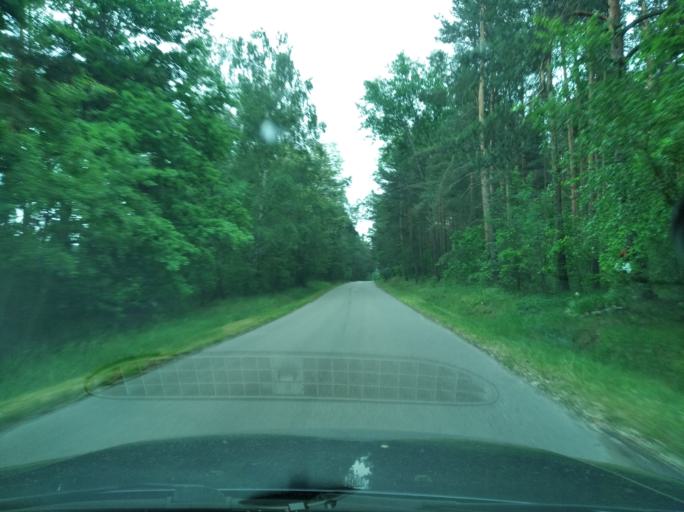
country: PL
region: Subcarpathian Voivodeship
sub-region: Powiat kolbuszowski
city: Niwiska
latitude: 50.2168
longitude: 21.6427
